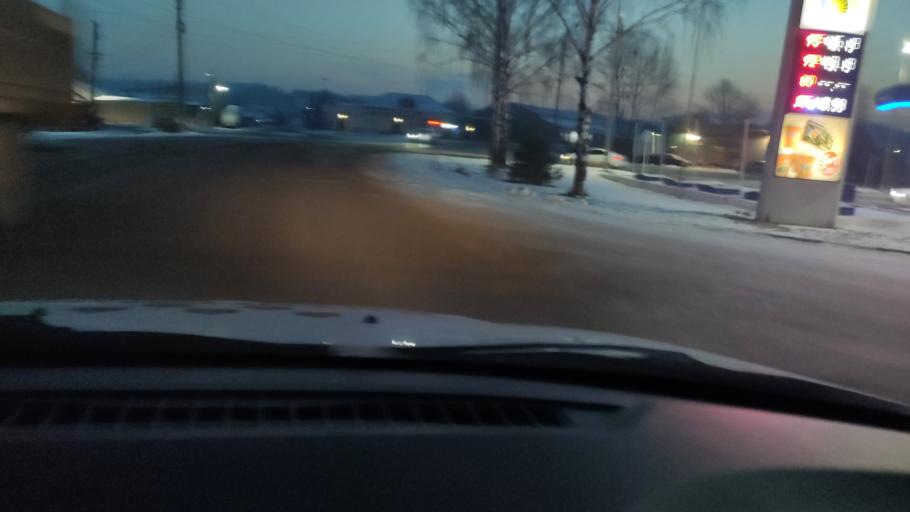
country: RU
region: Perm
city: Kungur
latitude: 57.4260
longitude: 56.9318
